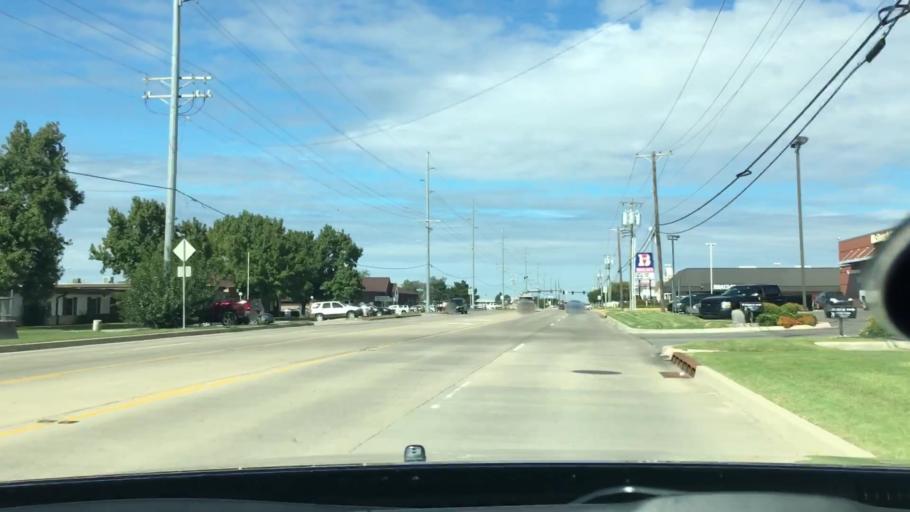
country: US
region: Oklahoma
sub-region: Pontotoc County
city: Ada
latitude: 34.7825
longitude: -96.6523
